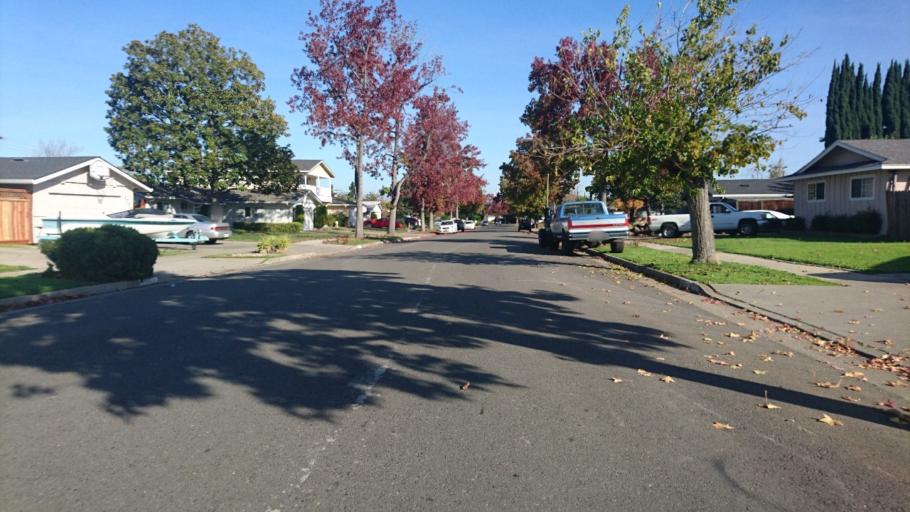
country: US
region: California
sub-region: Santa Clara County
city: Cambrian Park
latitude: 37.2540
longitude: -121.9171
